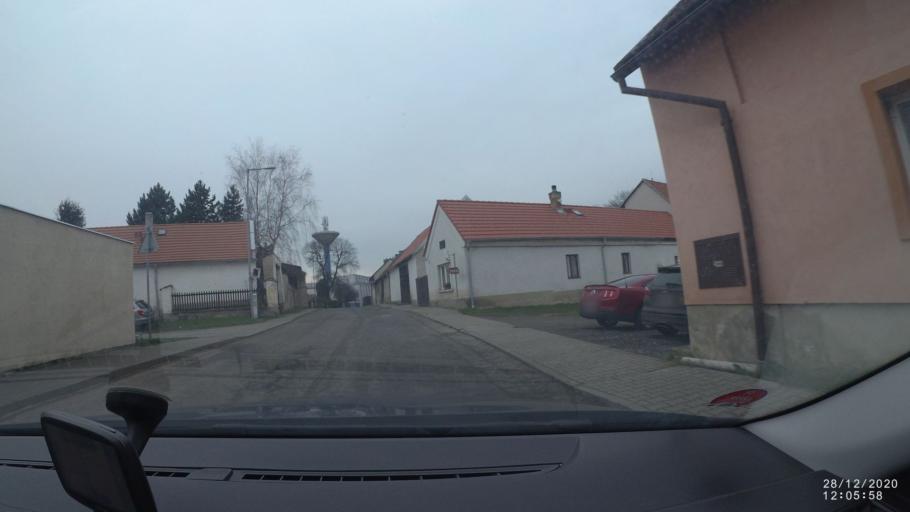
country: CZ
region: Central Bohemia
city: Brandys nad Labem-Stara Boleslav
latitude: 50.1616
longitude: 14.6741
